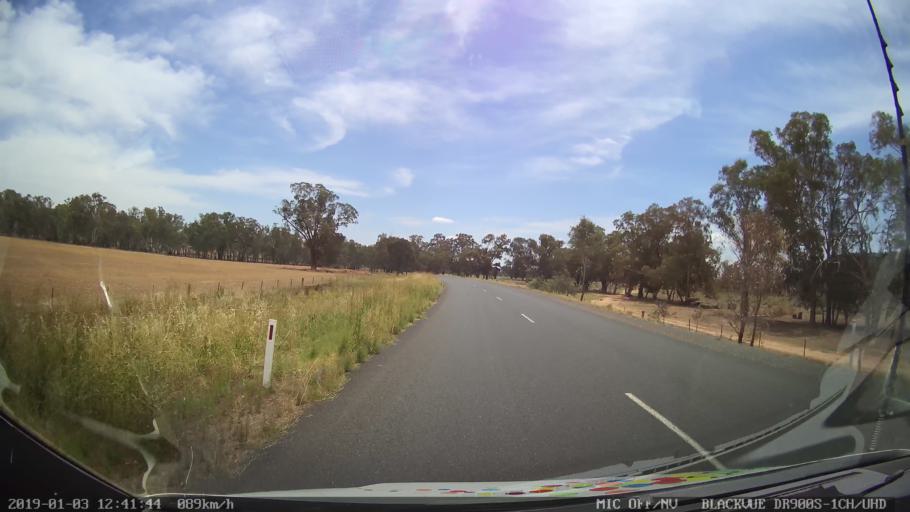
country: AU
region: New South Wales
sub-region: Weddin
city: Grenfell
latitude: -33.7957
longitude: 148.2154
